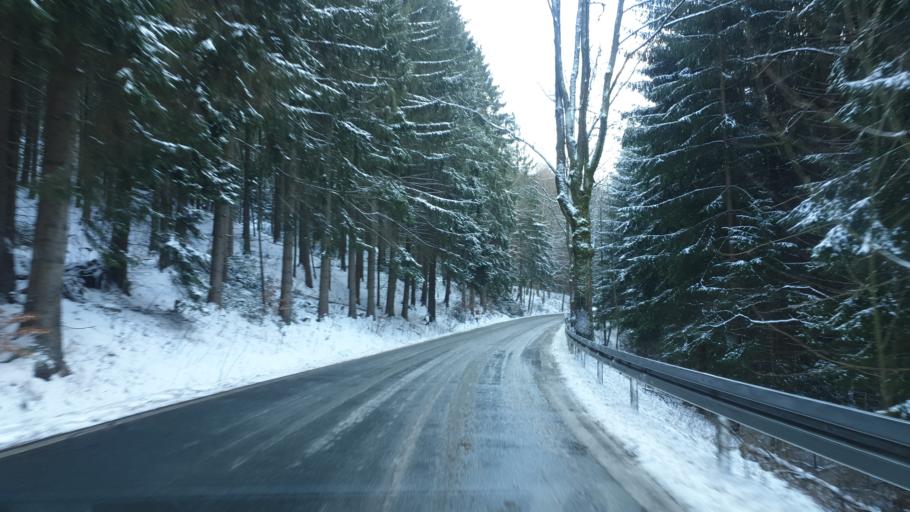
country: DE
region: Saxony
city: Bad Elster
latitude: 50.2706
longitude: 12.2502
